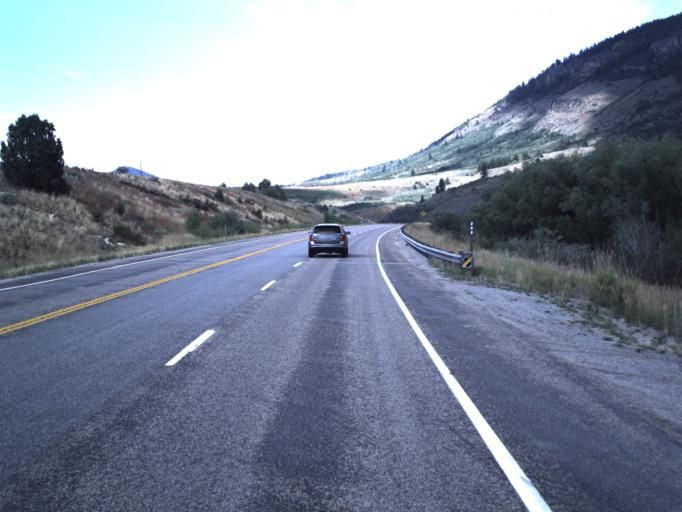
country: US
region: Utah
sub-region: Cache County
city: Richmond
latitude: 41.8762
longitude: -111.5651
